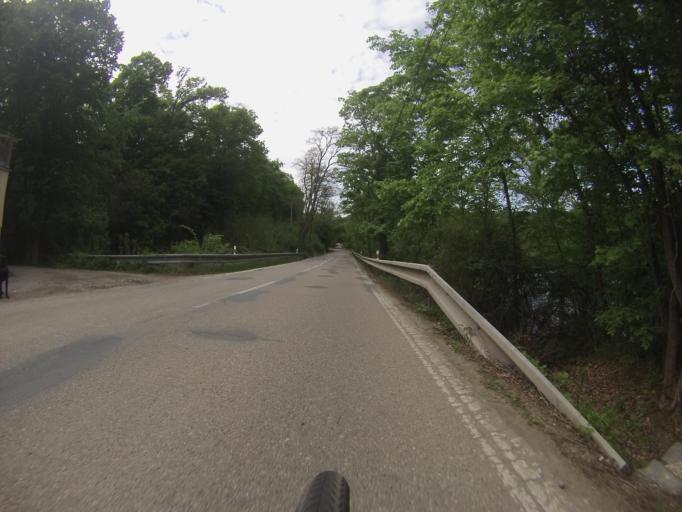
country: CZ
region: South Moravian
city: Kurim
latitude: 49.2460
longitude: 16.4960
